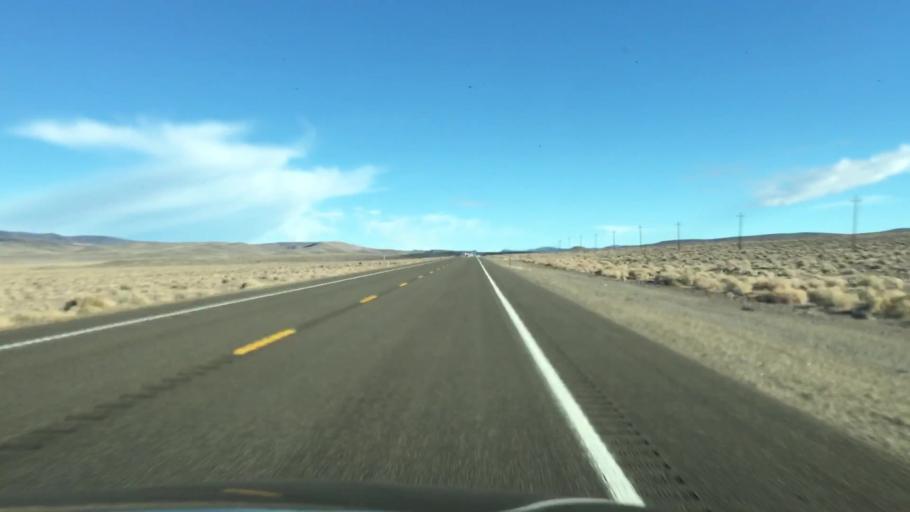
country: US
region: Nevada
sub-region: Mineral County
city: Hawthorne
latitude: 38.2520
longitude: -118.0752
